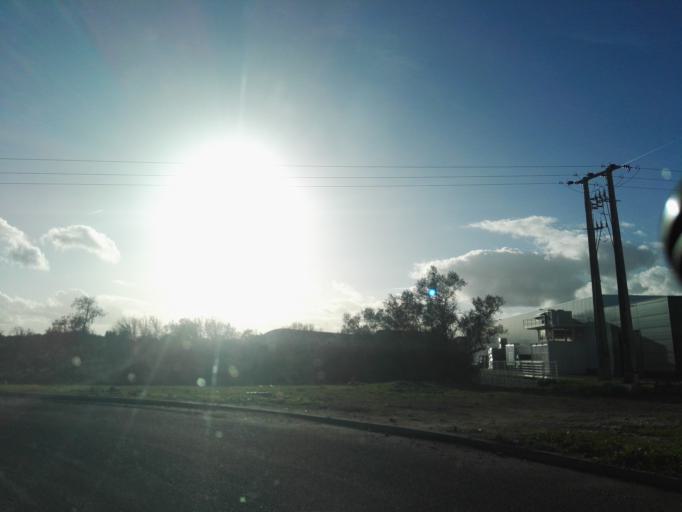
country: PT
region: Portalegre
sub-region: Elvas
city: Elvas
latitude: 38.8740
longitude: -7.1858
